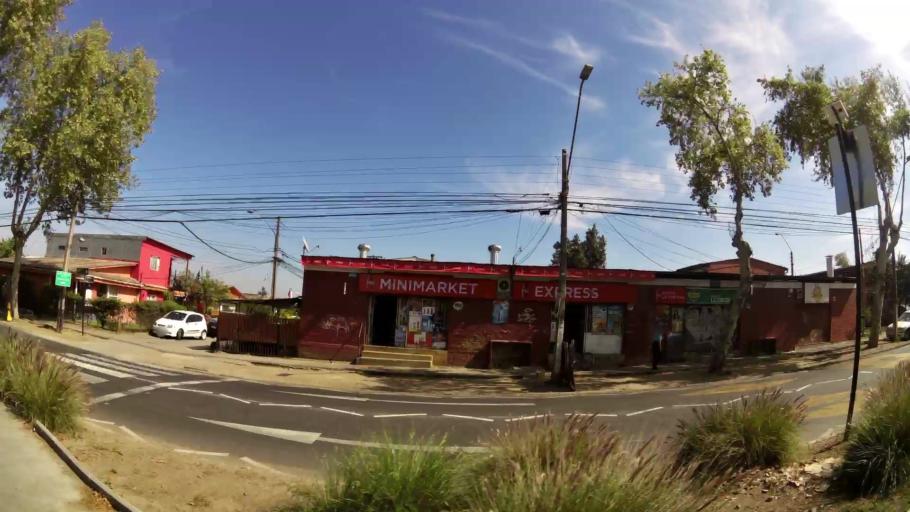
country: CL
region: Santiago Metropolitan
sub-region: Provincia de Santiago
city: Villa Presidente Frei, Nunoa, Santiago, Chile
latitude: -33.4475
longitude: -70.5383
